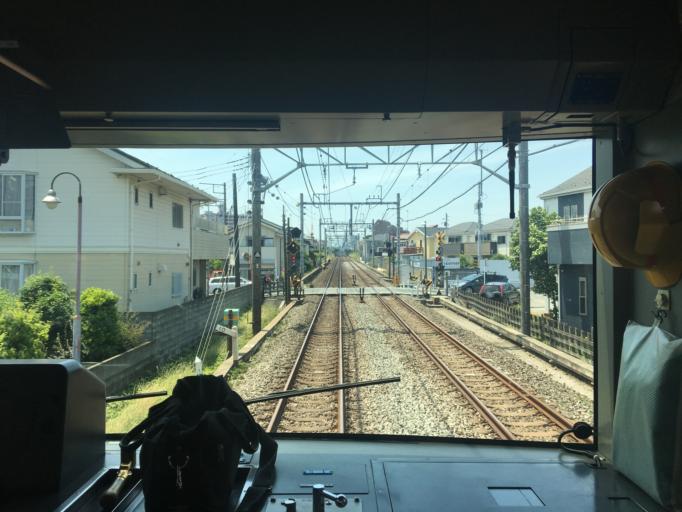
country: JP
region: Saitama
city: Tokorozawa
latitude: 35.7770
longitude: 139.5024
